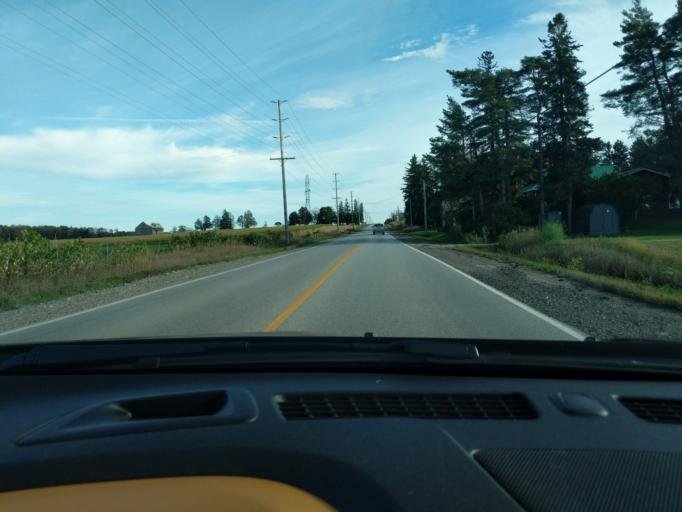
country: CA
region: Ontario
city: Barrie
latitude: 44.4117
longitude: -79.7511
